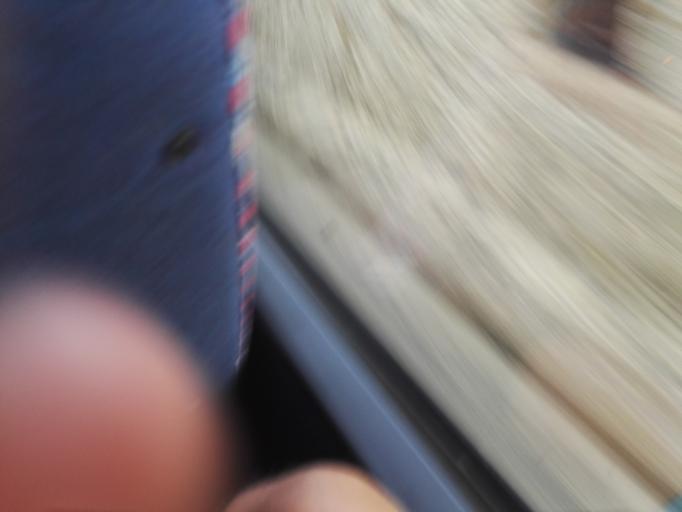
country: IT
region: Calabria
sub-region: Provincia di Reggio Calabria
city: Bova Marina
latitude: 37.9254
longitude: 15.9408
